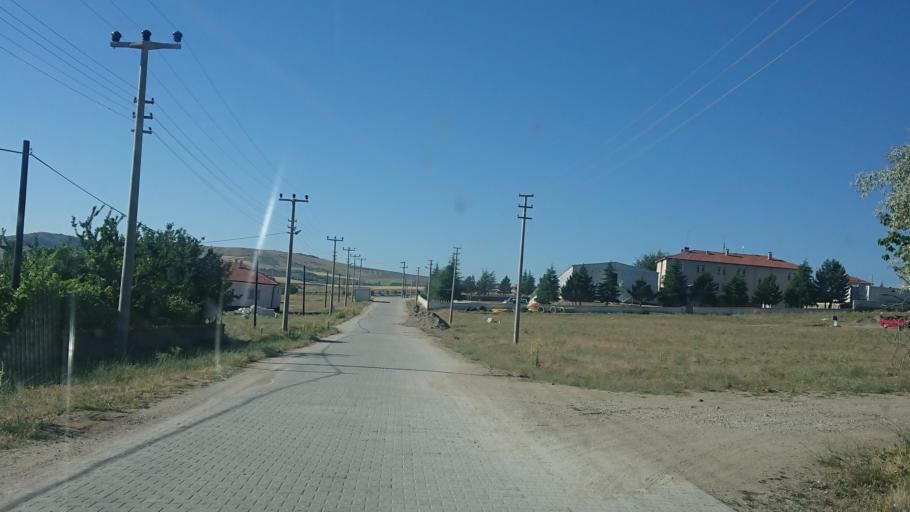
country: TR
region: Aksaray
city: Agacoren
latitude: 38.8713
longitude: 33.9449
